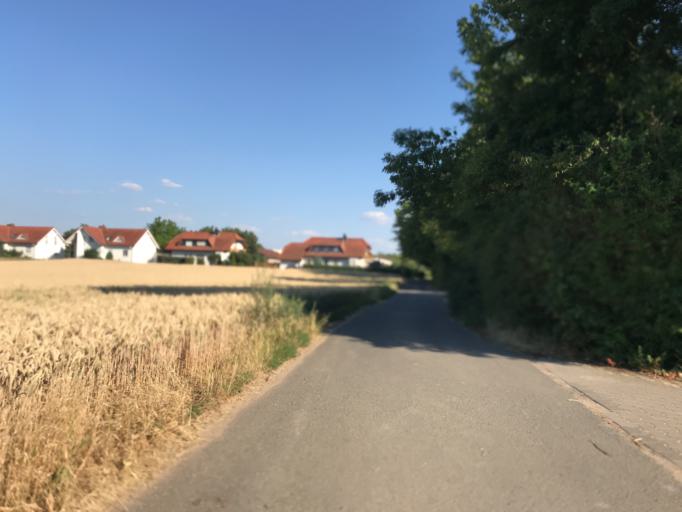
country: DE
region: Rheinland-Pfalz
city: Klein-Winternheim
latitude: 49.9778
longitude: 8.2318
